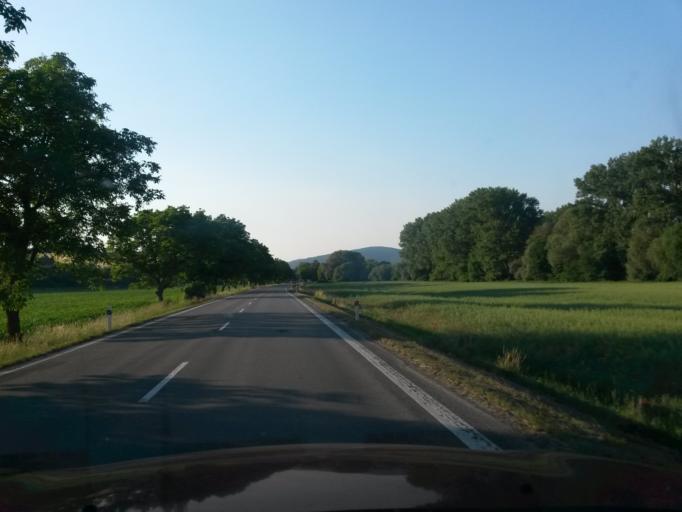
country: SK
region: Presovsky
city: Vranov nad Topl'ou
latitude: 48.9779
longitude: 21.5785
